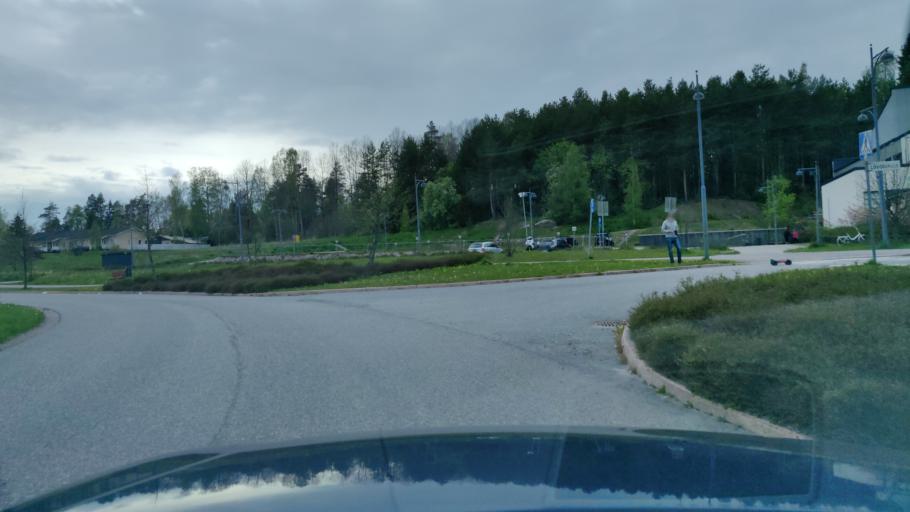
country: FI
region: Uusimaa
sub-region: Helsinki
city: Nurmijaervi
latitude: 60.3851
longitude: 24.7589
